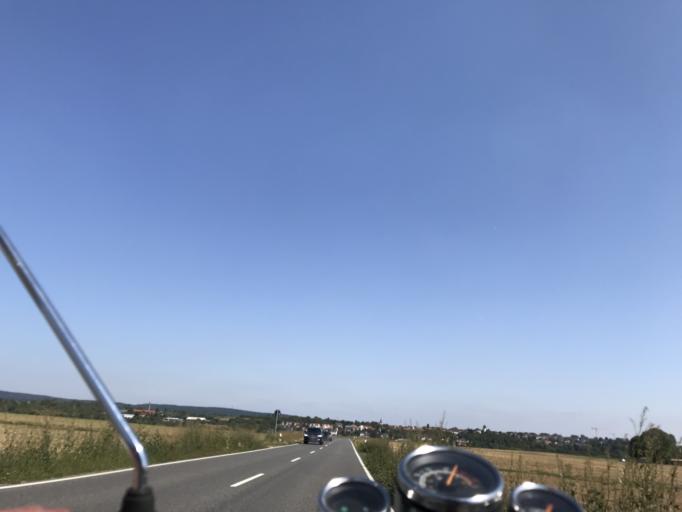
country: DE
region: Hesse
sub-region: Regierungsbezirk Darmstadt
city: Wiesbaden
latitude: 50.0820
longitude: 8.3060
